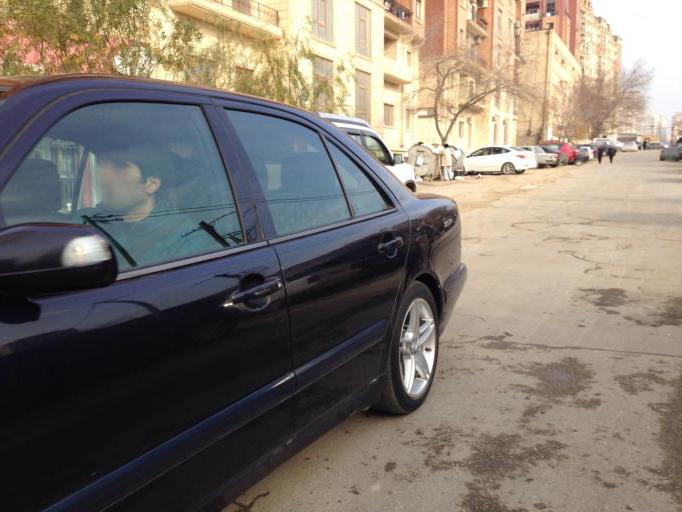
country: AZ
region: Baki
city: Baku
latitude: 40.3983
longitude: 49.8612
